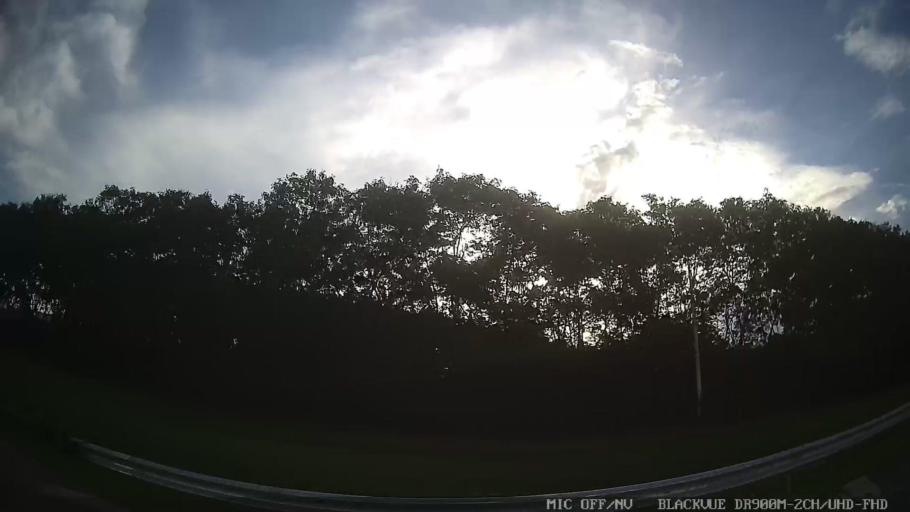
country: BR
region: Sao Paulo
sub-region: Tiete
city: Tiete
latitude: -23.1254
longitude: -47.6982
